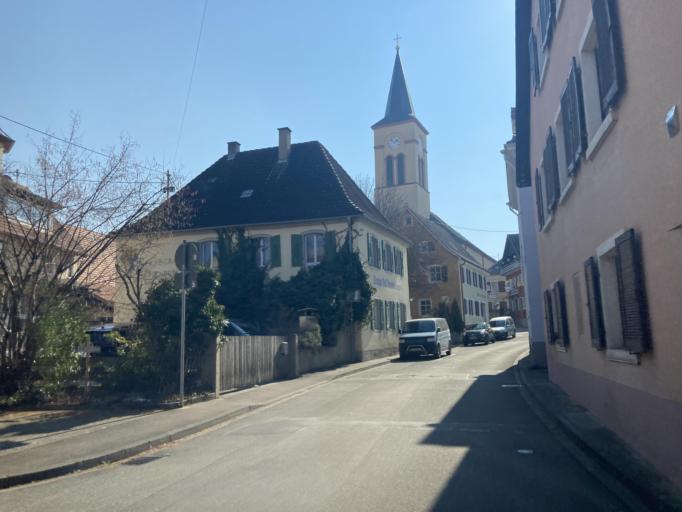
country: DE
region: Baden-Wuerttemberg
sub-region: Freiburg Region
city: Vogtsburg
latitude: 48.0896
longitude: 7.6301
